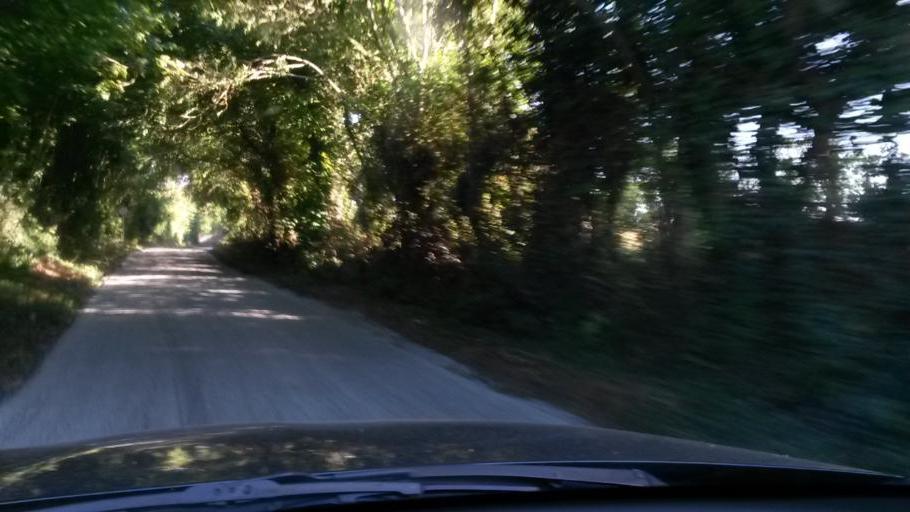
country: IE
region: Leinster
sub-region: An Mhi
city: Ashbourne
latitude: 53.4932
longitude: -6.3061
